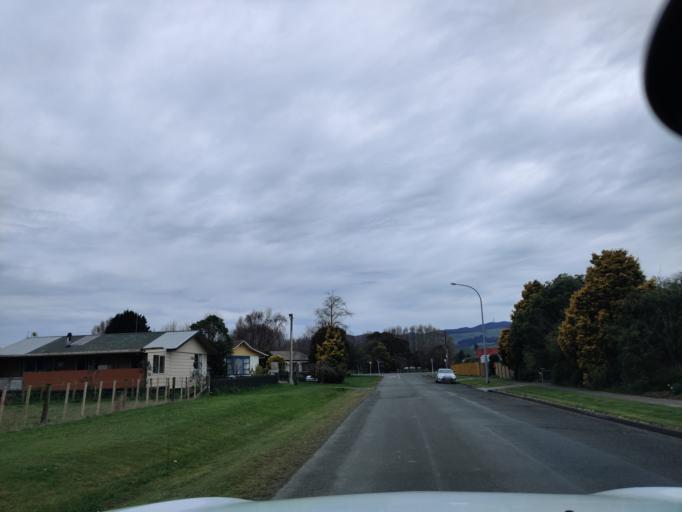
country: NZ
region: Manawatu-Wanganui
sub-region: Palmerston North City
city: Palmerston North
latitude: -40.2845
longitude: 175.7496
